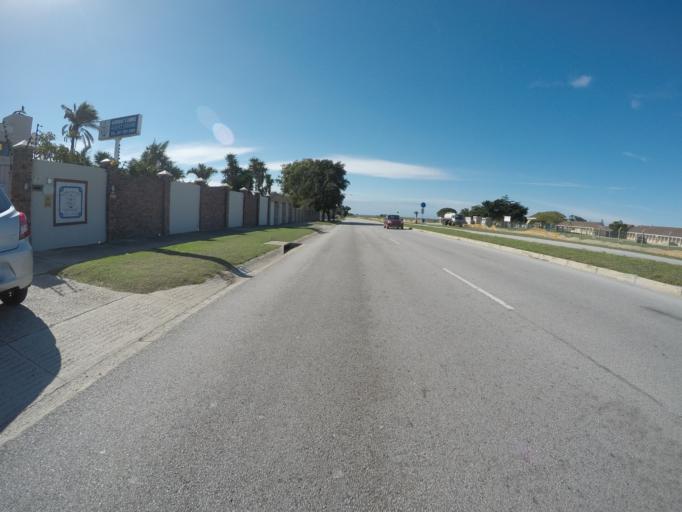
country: ZA
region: Eastern Cape
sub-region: Nelson Mandela Bay Metropolitan Municipality
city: Port Elizabeth
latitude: -33.9964
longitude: 25.6669
